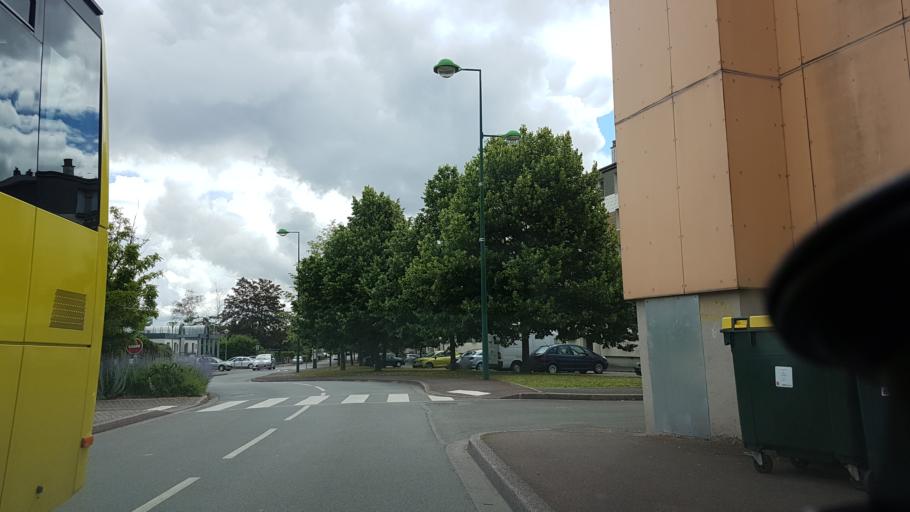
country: FR
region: Centre
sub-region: Departement du Cher
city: Saint-Doulchard
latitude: 47.1055
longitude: 2.3760
